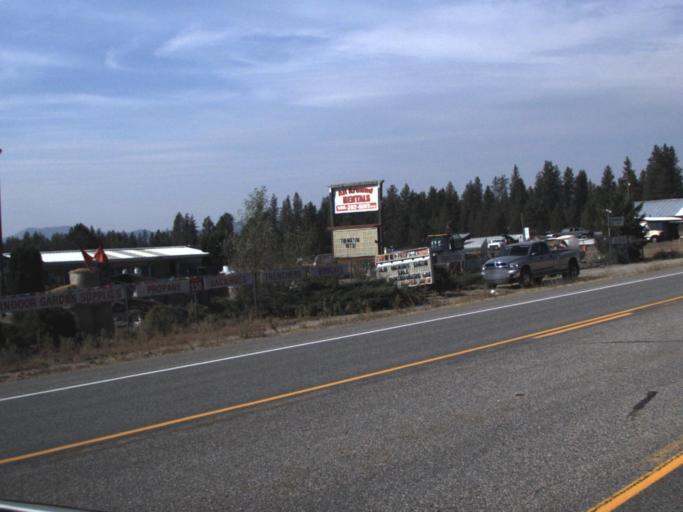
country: US
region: Washington
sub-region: Spokane County
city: Deer Park
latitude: 48.0142
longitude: -117.3495
